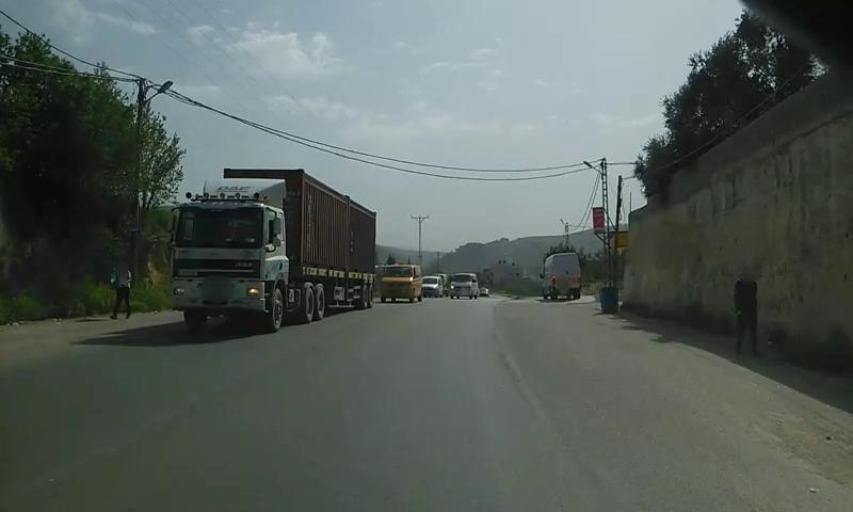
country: PS
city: Bir al Basha
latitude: 32.4192
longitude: 35.2304
